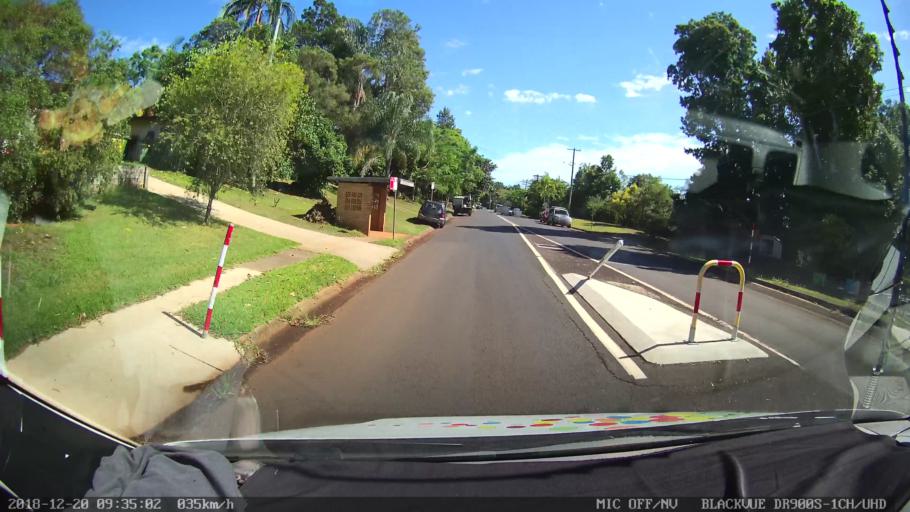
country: AU
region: New South Wales
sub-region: Lismore Municipality
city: Nimbin
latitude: -28.6866
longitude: 153.3148
